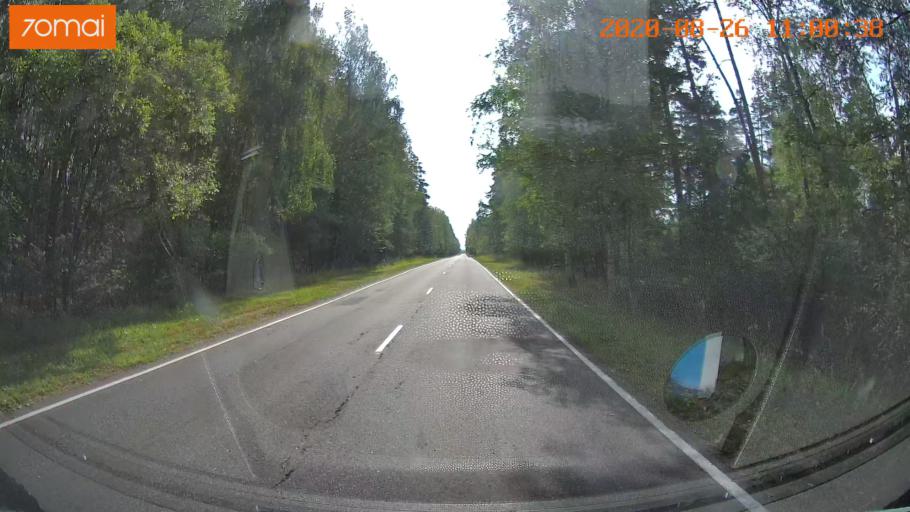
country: RU
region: Rjazan
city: Izhevskoye
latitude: 54.5728
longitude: 41.2151
